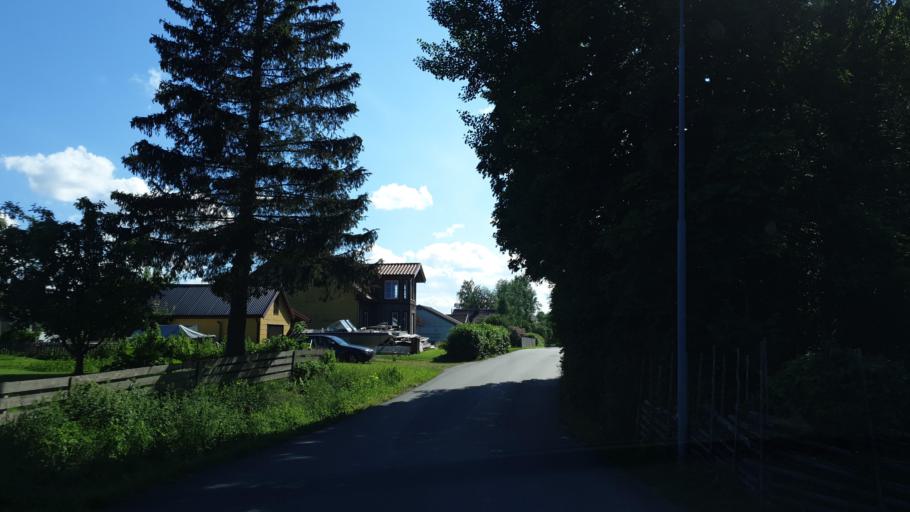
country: SE
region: Dalarna
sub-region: Avesta Kommun
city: Avesta
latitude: 60.1283
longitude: 16.2568
